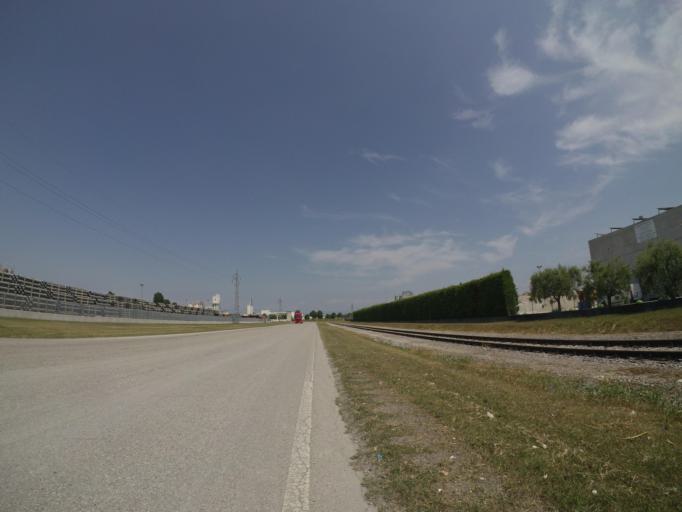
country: IT
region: Friuli Venezia Giulia
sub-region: Provincia di Pordenone
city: Rosa
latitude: 45.9445
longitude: 12.8873
